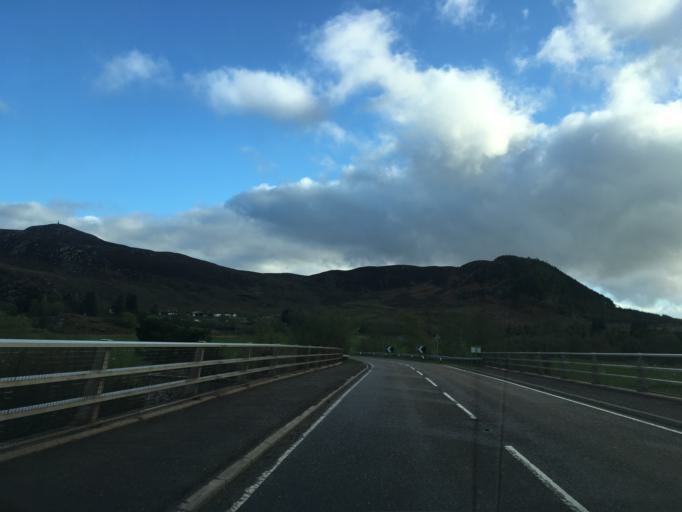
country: GB
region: Scotland
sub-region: Highland
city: Kingussie
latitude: 57.0189
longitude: -4.2836
